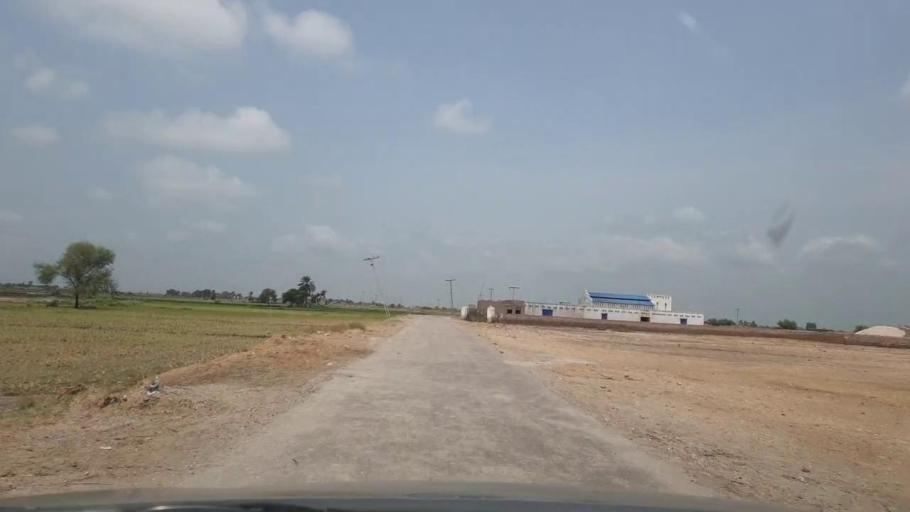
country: PK
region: Sindh
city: Ratodero
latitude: 27.9018
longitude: 68.3211
